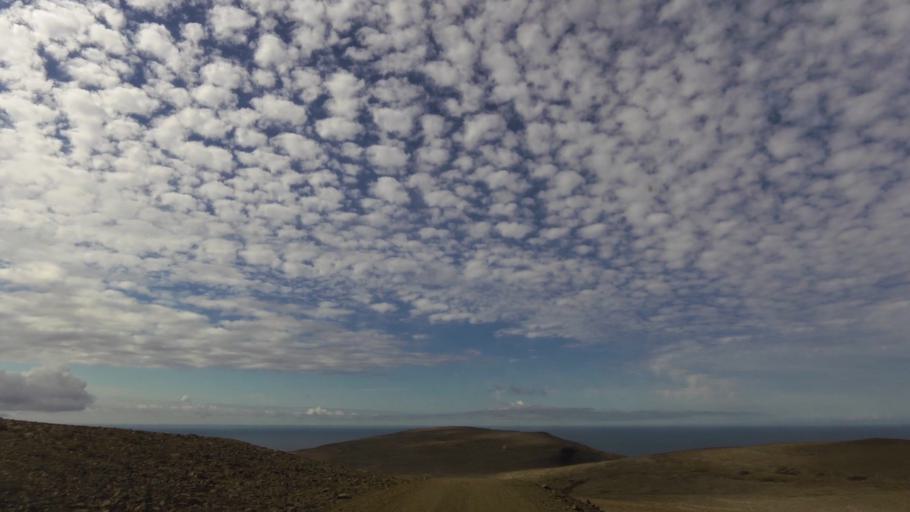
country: IS
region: West
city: Olafsvik
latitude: 65.6217
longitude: -24.2798
